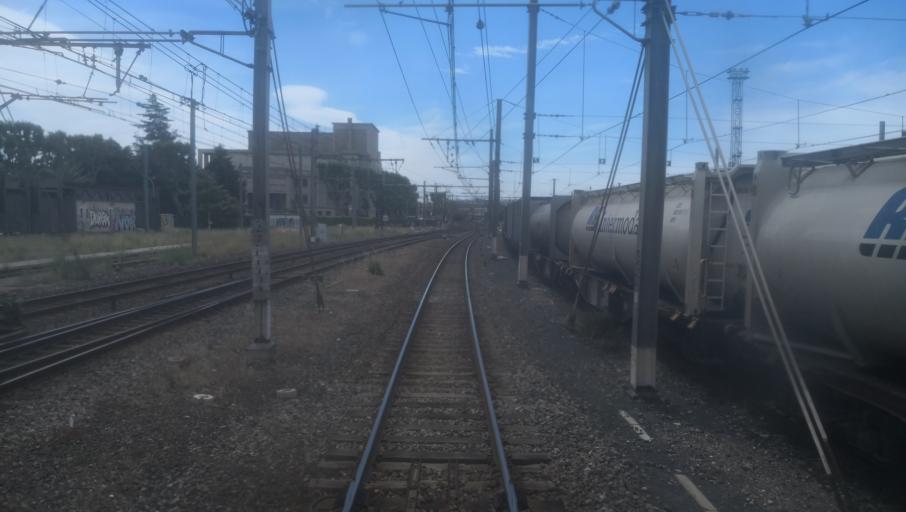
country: FR
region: Languedoc-Roussillon
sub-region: Departement de l'Aude
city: Narbonne
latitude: 43.1882
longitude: 3.0030
